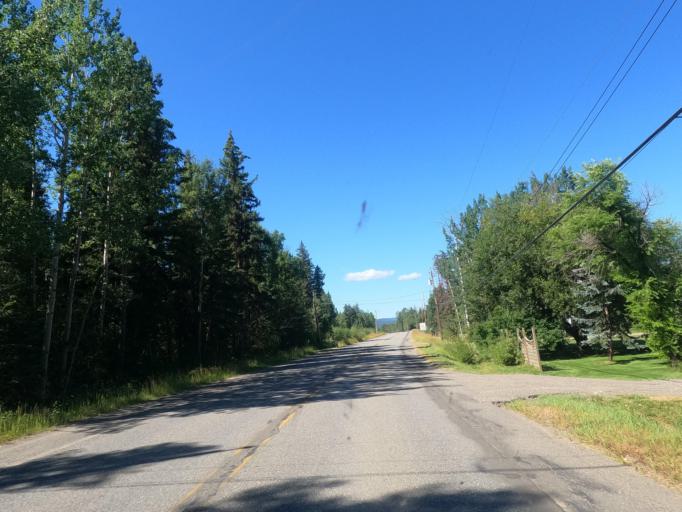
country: CA
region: British Columbia
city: Quesnel
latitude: 53.0217
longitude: -122.4517
